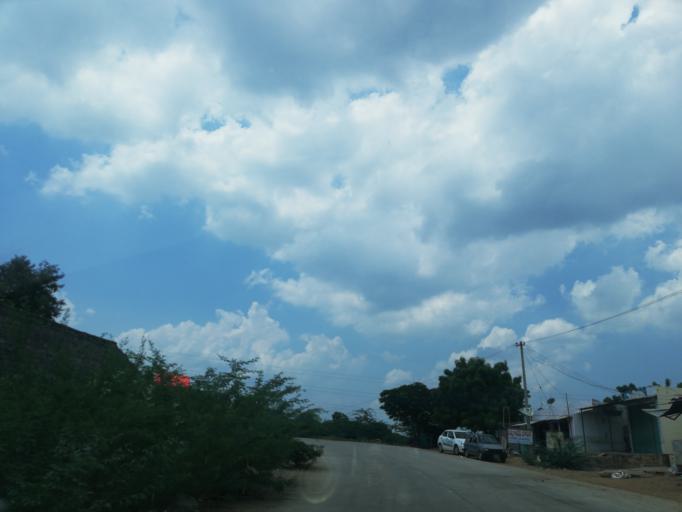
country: IN
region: Andhra Pradesh
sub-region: Guntur
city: Macherla
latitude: 16.5824
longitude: 79.3284
